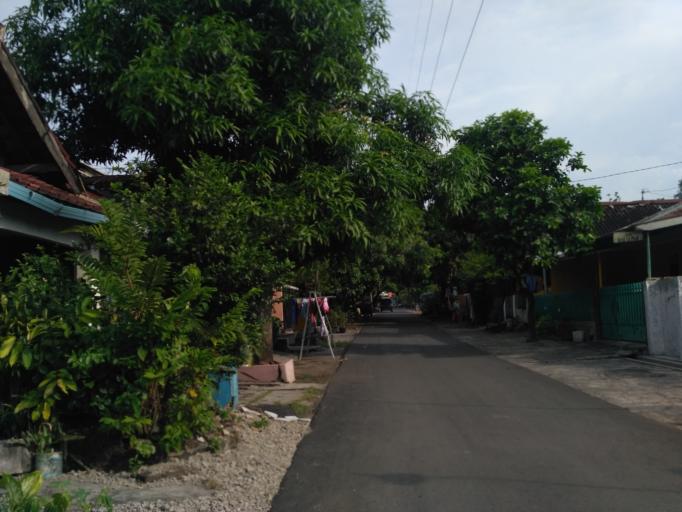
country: ID
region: Central Java
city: Semarang
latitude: -7.0152
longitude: 110.4442
